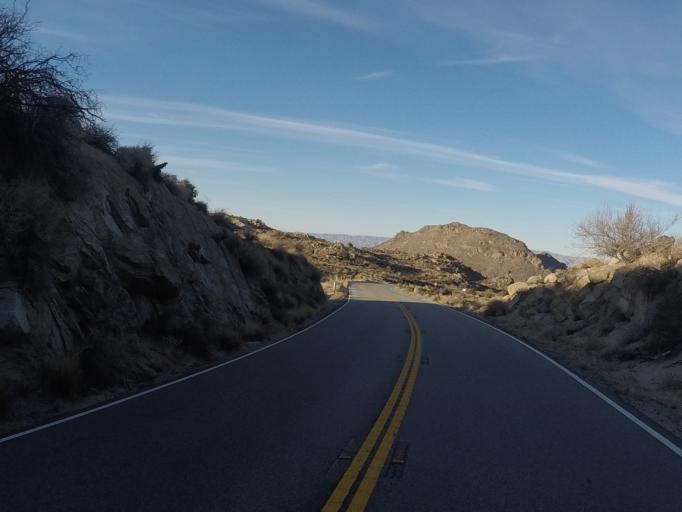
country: US
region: California
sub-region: Riverside County
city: La Quinta
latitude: 33.6097
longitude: -116.4159
